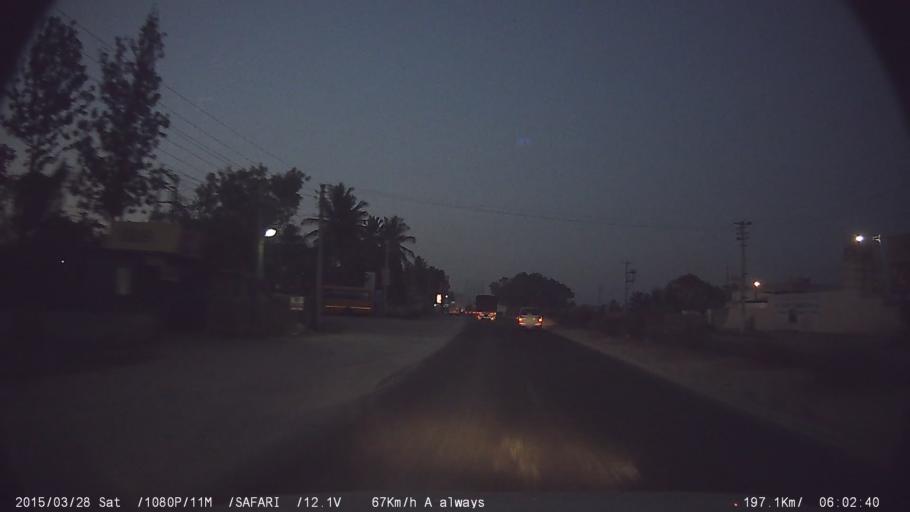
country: IN
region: Karnataka
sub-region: Ramanagara
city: Ramanagaram
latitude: 12.8458
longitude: 77.4222
